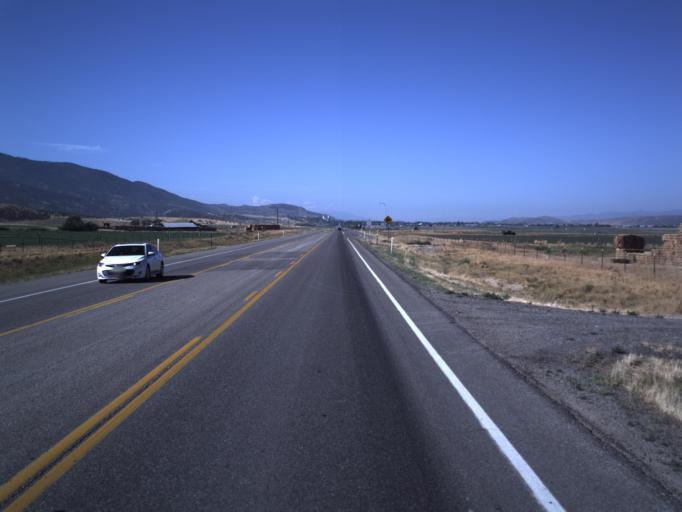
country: US
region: Utah
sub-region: Sanpete County
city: Ephraim
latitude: 39.3282
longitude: -111.6016
